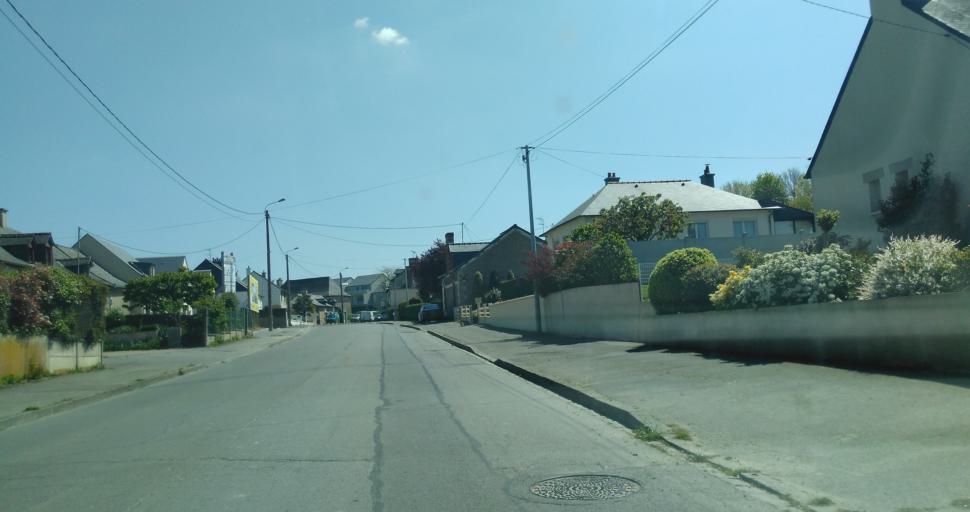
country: FR
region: Brittany
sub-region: Departement d'Ille-et-Vilaine
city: Saint-Gilles
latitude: 48.1281
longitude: -1.8213
